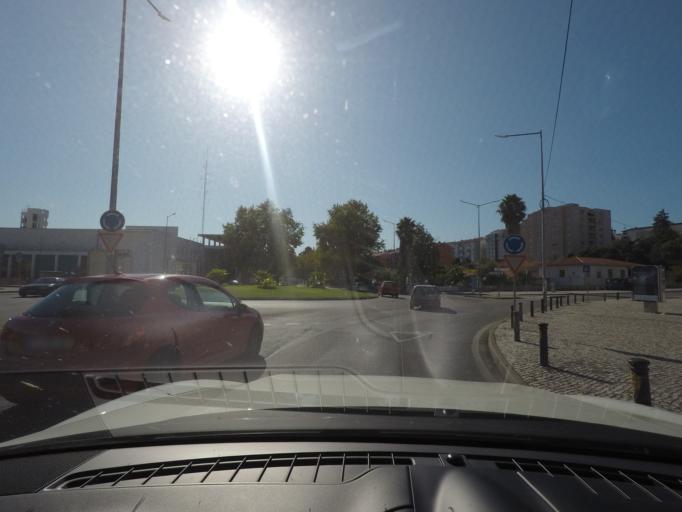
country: PT
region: Coimbra
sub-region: Coimbra
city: Coimbra
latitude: 40.1947
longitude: -8.4122
